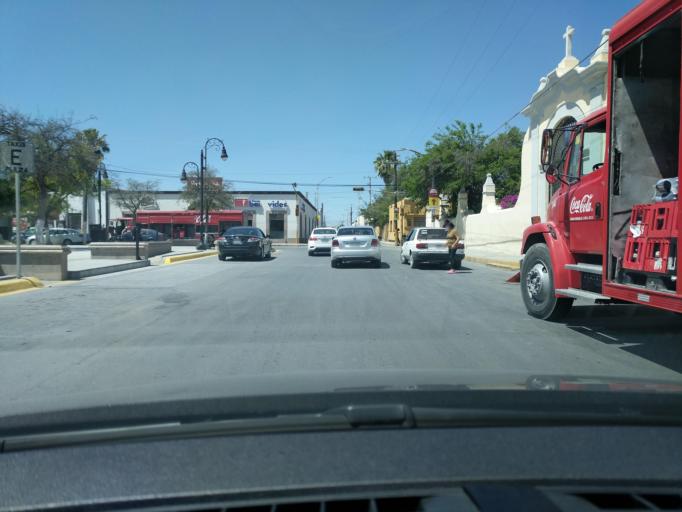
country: MX
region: Nuevo Leon
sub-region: Salinas Victoria
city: Las Torres
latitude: 25.9602
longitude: -100.2906
